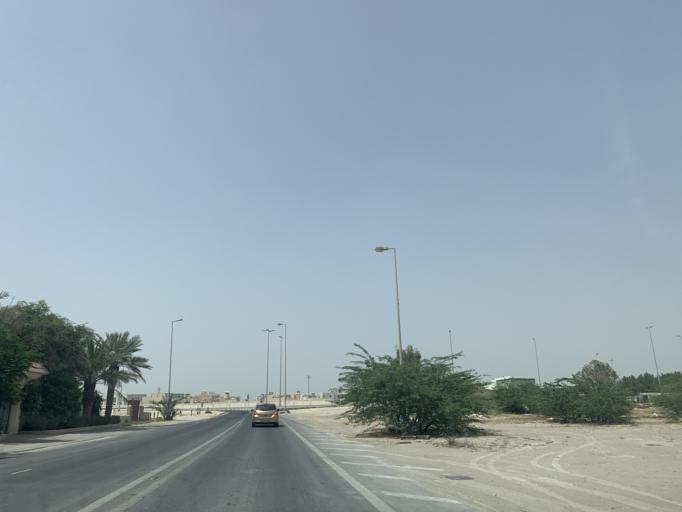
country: BH
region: Northern
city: Madinat `Isa
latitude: 26.1582
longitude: 50.5259
